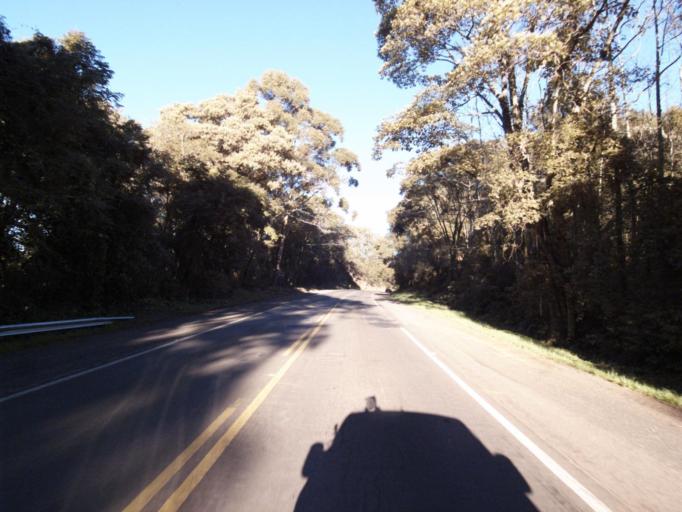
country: BR
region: Santa Catarina
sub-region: Sao Lourenco Do Oeste
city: Sao Lourenco dOeste
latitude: -26.7685
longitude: -53.2620
